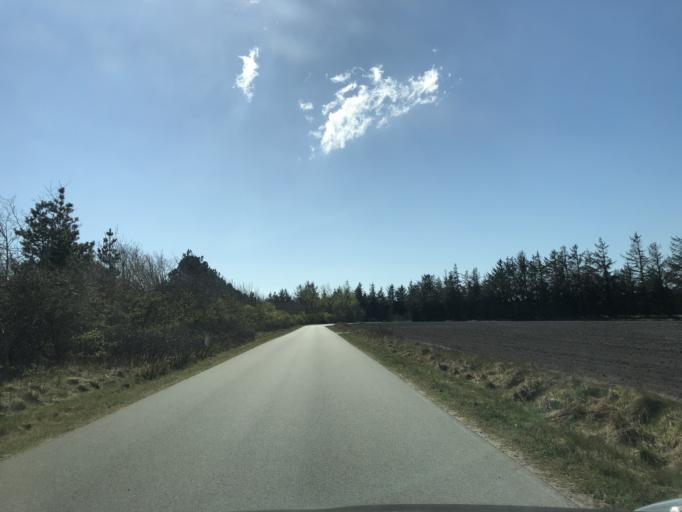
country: DK
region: Central Jutland
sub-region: Holstebro Kommune
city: Ulfborg
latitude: 56.3167
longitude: 8.1964
